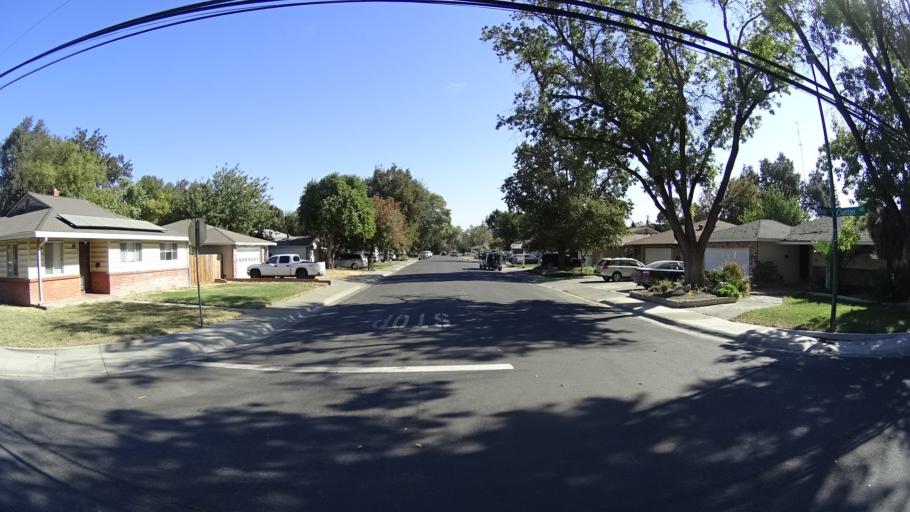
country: US
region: California
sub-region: Yolo County
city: Woodland
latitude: 38.6711
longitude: -121.7841
